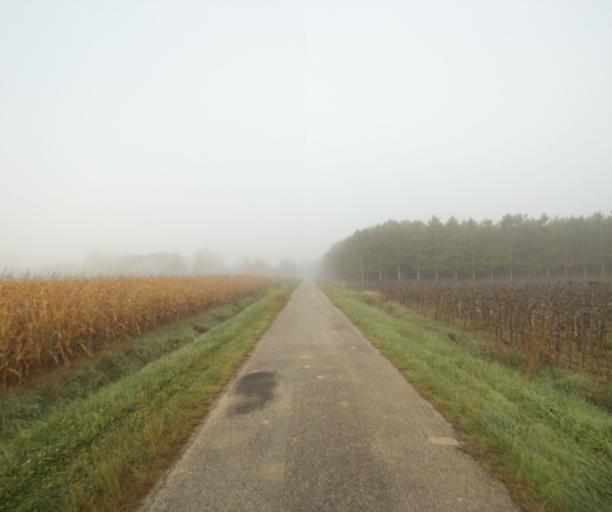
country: FR
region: Midi-Pyrenees
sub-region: Departement du Tarn-et-Garonne
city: Nohic
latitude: 43.8945
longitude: 1.4483
